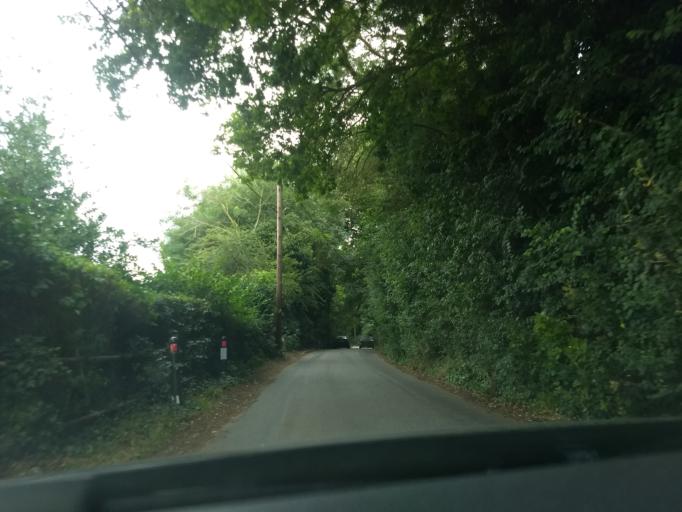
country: GB
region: England
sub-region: Suffolk
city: Shotley Gate
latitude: 51.9913
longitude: 1.2128
